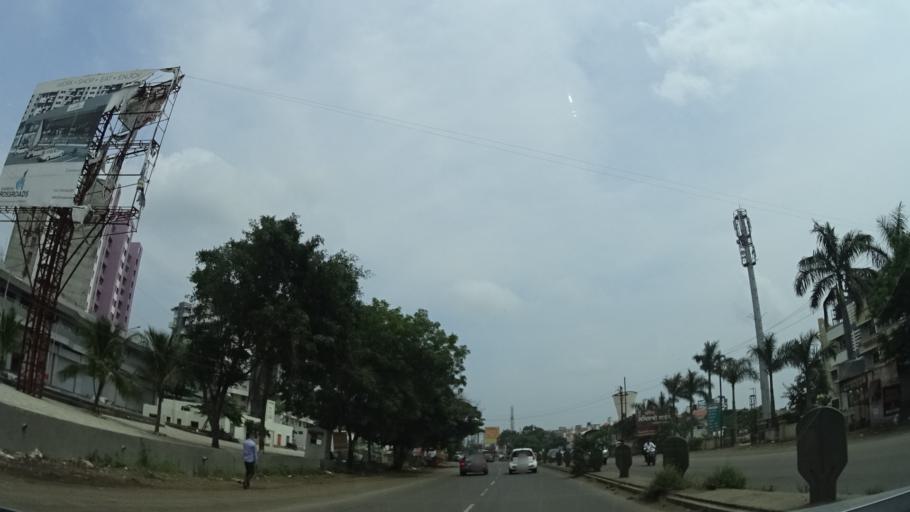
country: IN
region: Maharashtra
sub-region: Pune Division
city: Lohogaon
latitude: 18.5888
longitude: 73.9967
